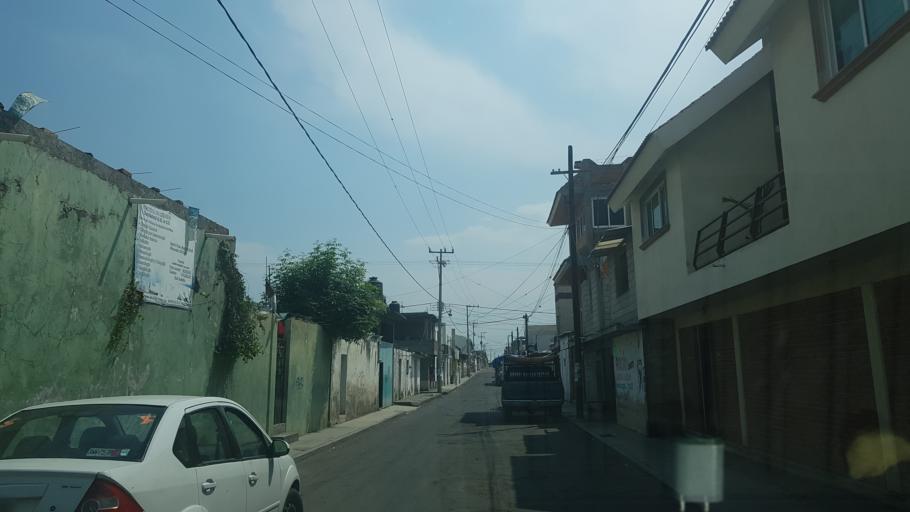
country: MX
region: Puebla
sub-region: Tianguismanalco
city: San Martin Tlapala
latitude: 18.9749
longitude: -98.4486
